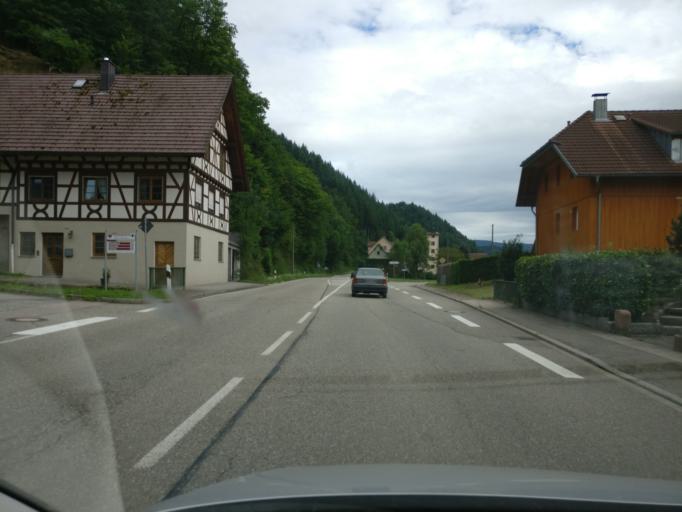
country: DE
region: Baden-Wuerttemberg
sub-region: Freiburg Region
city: Oppenau
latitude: 48.4898
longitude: 8.1472
